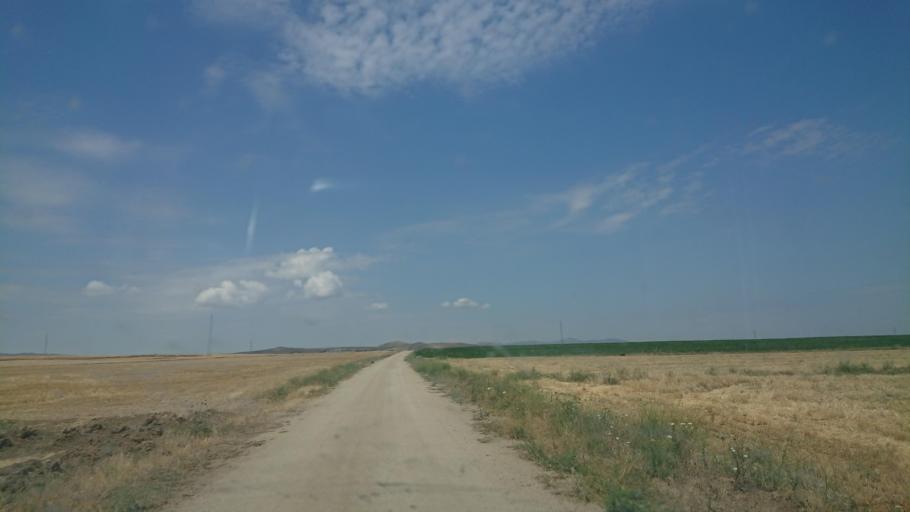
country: TR
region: Aksaray
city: Agacoren
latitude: 38.9560
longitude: 33.9179
